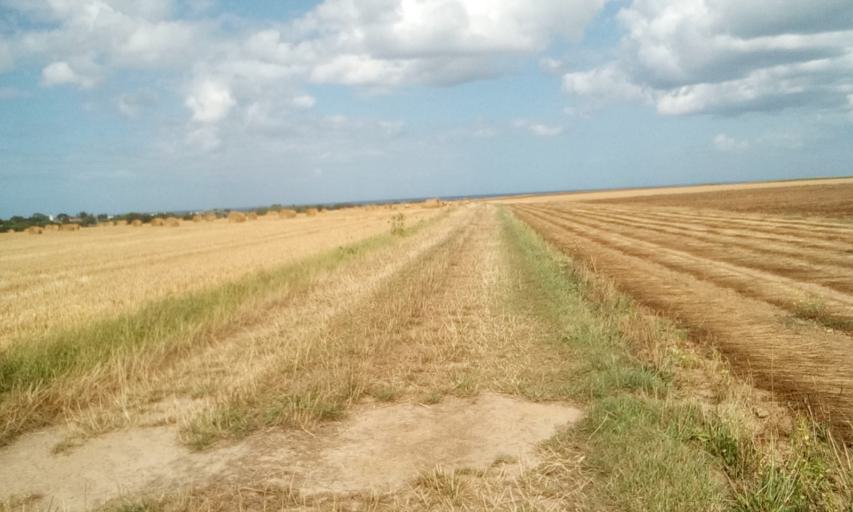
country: FR
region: Lower Normandy
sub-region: Departement du Calvados
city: Ver-sur-Mer
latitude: 49.3282
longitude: -0.5228
